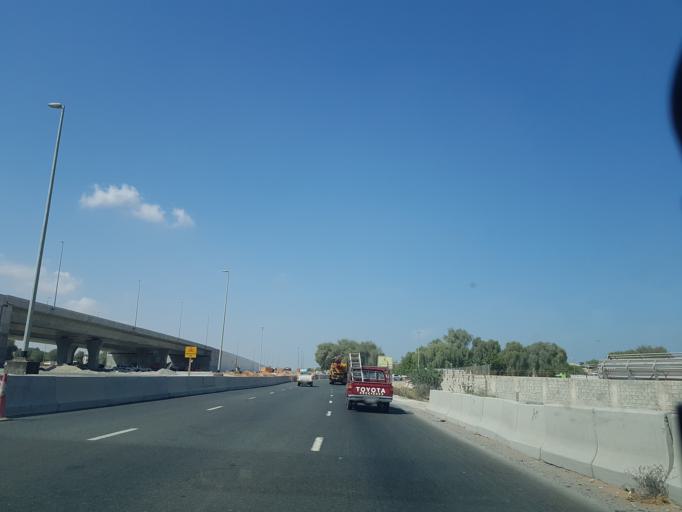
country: AE
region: Ra's al Khaymah
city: Ras al-Khaimah
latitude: 25.7001
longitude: 55.9692
